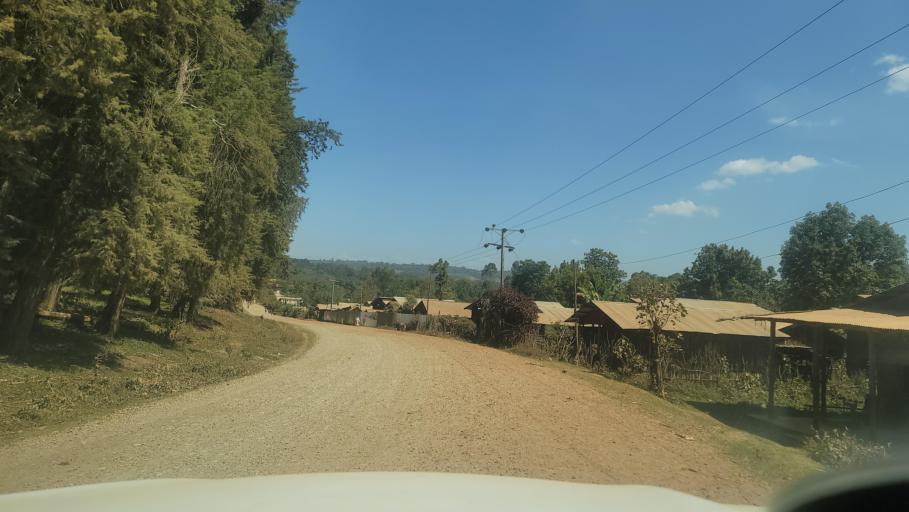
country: ET
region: Oromiya
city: Agaro
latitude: 7.7838
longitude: 36.4110
